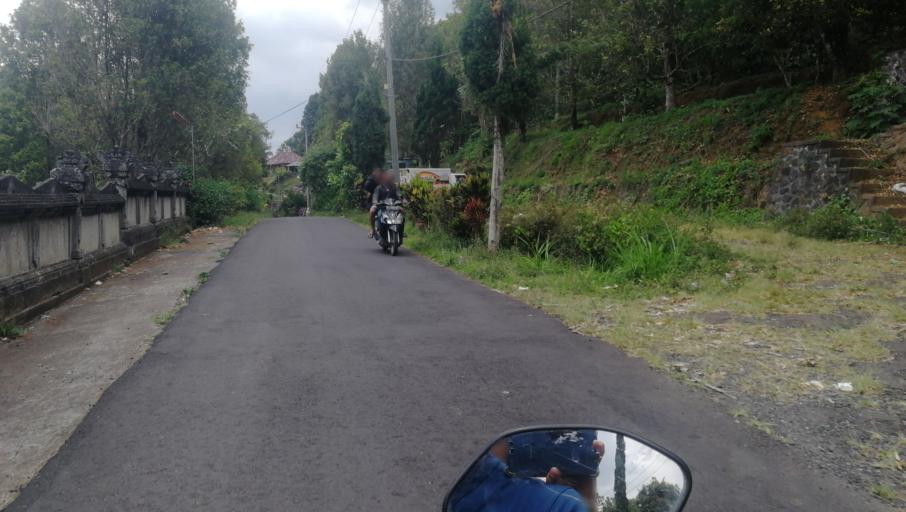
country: ID
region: Bali
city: Munduk
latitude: -8.2887
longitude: 115.0413
